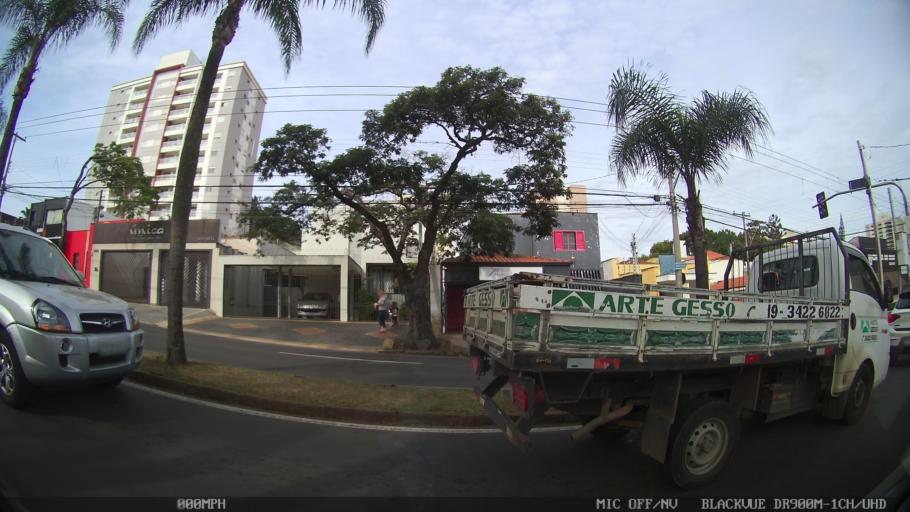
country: BR
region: Sao Paulo
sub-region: Piracicaba
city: Piracicaba
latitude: -22.7340
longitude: -47.6387
